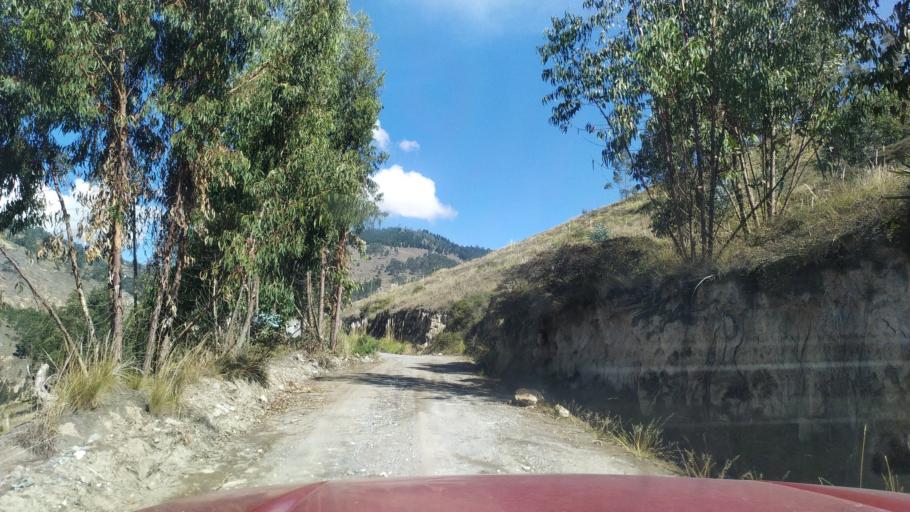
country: EC
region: Chimborazo
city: Riobamba
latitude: -1.6756
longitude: -78.6962
